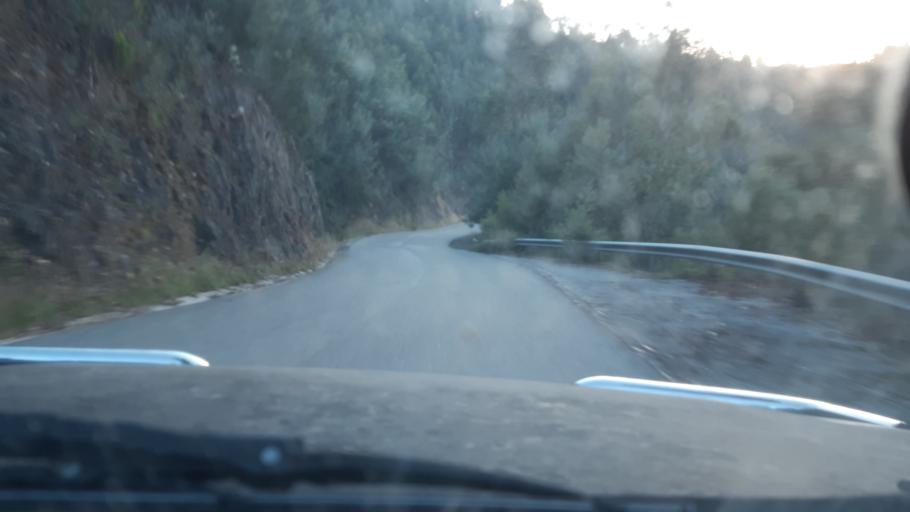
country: PT
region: Aveiro
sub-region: Agueda
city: Aguada de Cima
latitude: 40.5677
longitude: -8.3554
